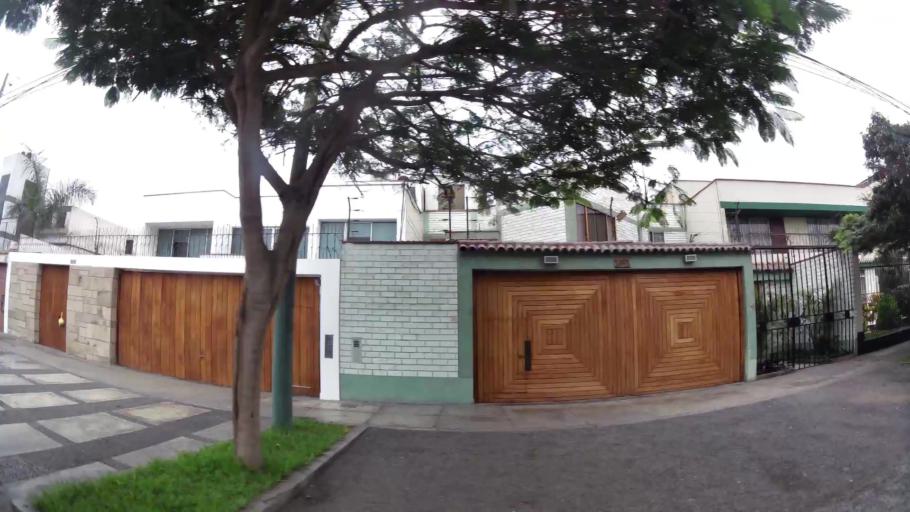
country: PE
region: Lima
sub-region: Lima
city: San Luis
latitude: -12.0903
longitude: -76.9879
